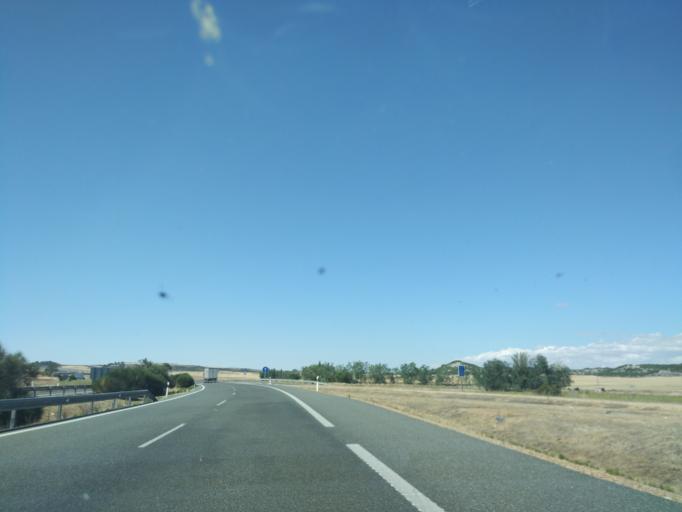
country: ES
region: Castille and Leon
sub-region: Provincia de Valladolid
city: Mota del Marques
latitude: 41.6377
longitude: -5.1876
